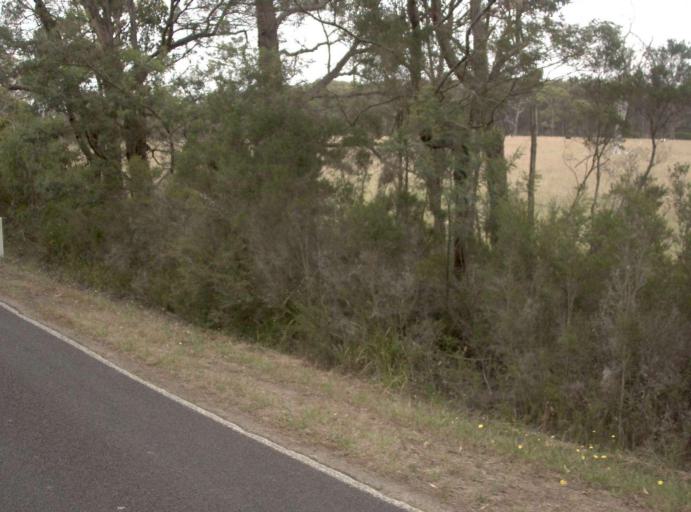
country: AU
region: Victoria
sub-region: Latrobe
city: Traralgon
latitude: -38.4974
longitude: 146.8332
